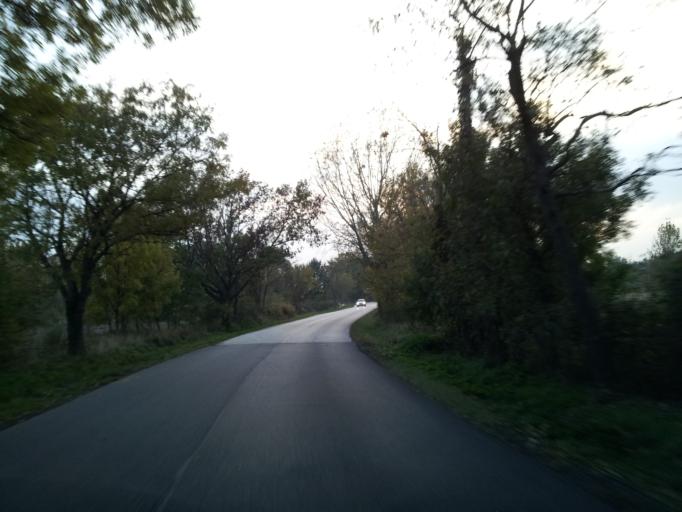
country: HU
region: Gyor-Moson-Sopron
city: Bakonyszentlaszlo
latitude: 47.4647
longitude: 17.8873
